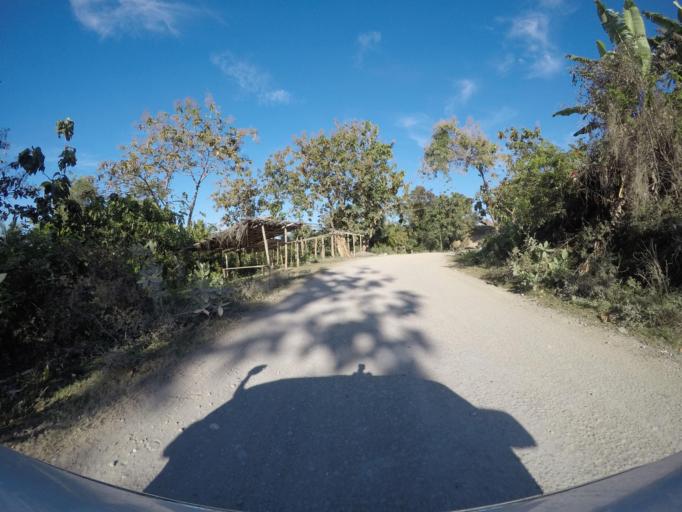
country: TL
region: Viqueque
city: Viqueque
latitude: -8.8664
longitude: 126.3353
